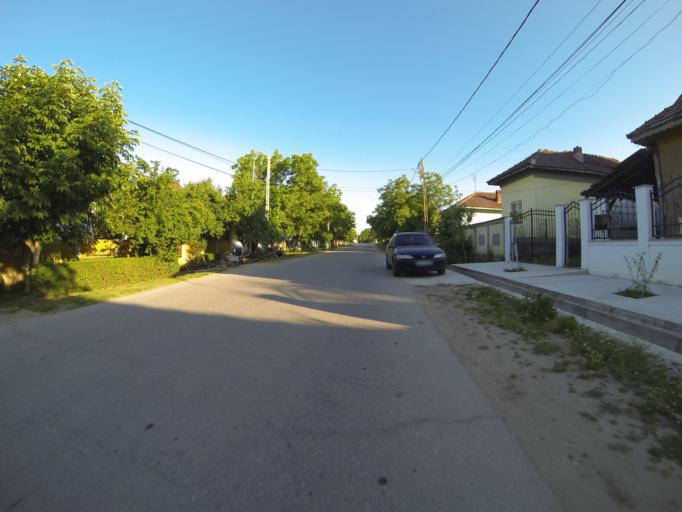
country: RO
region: Dolj
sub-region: Comuna Tuglui
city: Tuglui
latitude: 44.1916
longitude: 23.8085
